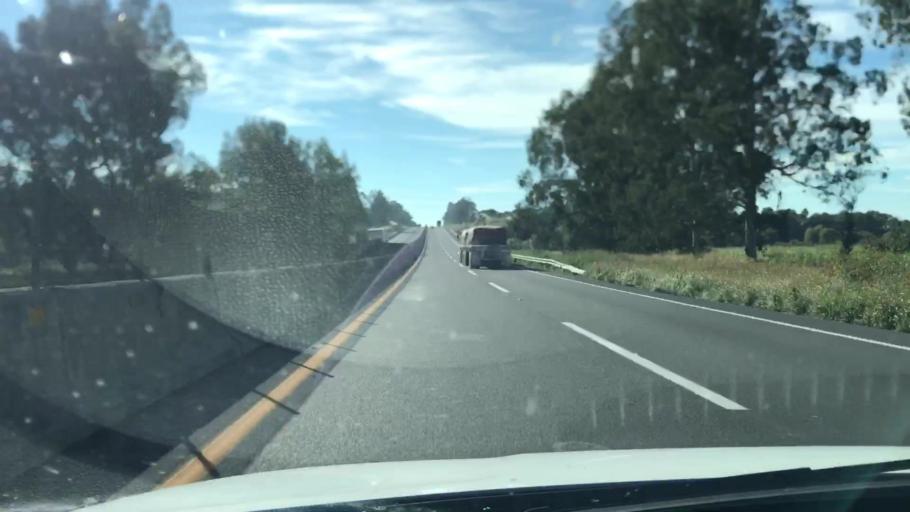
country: MX
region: Jalisco
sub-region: Lagos de Moreno
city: Cristeros [Fraccionamiento]
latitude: 21.3111
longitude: -102.0324
